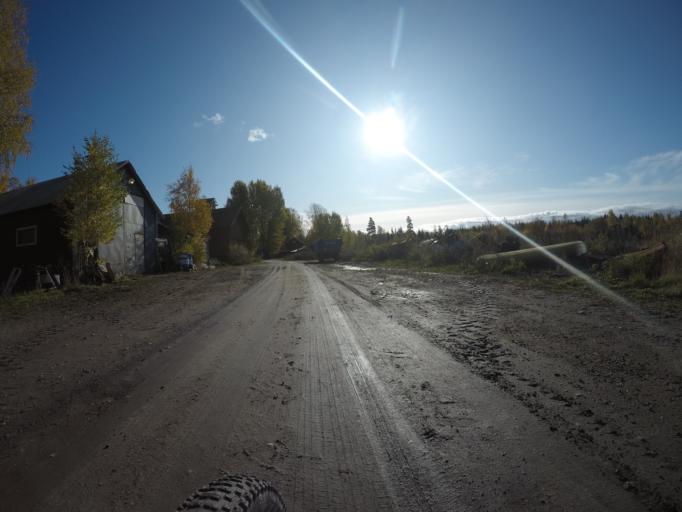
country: SE
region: Vaestmanland
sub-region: Kungsors Kommun
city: Kungsoer
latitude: 59.3164
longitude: 16.0975
